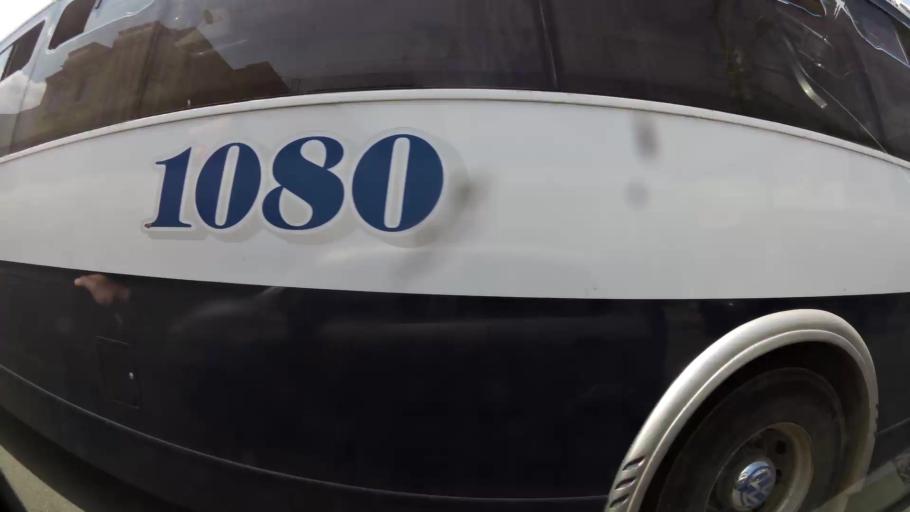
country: EC
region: Guayas
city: Eloy Alfaro
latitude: -2.1619
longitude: -79.8422
